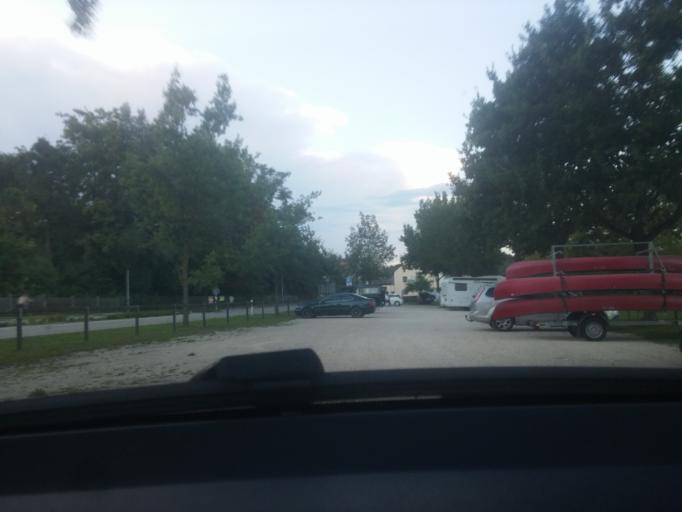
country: DE
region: Bavaria
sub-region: Upper Palatinate
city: Lappersdorf
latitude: 49.0668
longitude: 12.0900
